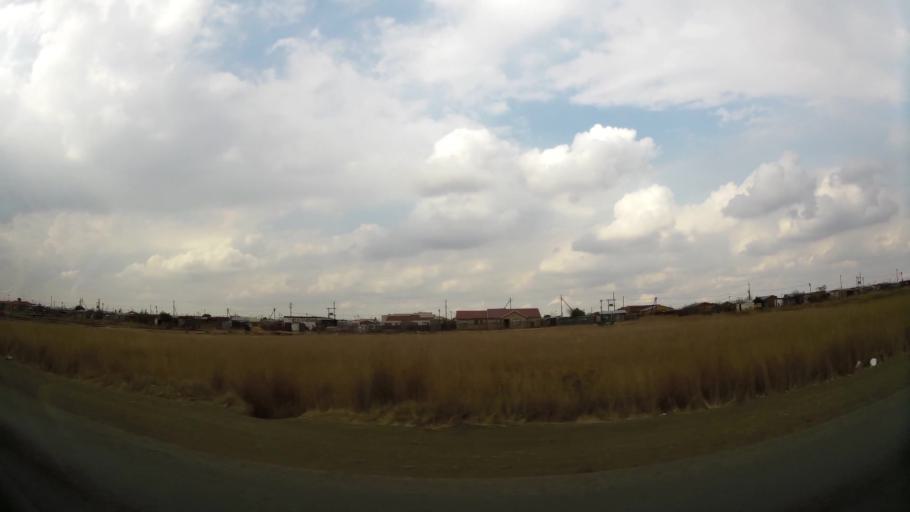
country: ZA
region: Orange Free State
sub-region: Fezile Dabi District Municipality
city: Sasolburg
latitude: -26.8584
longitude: 27.8883
